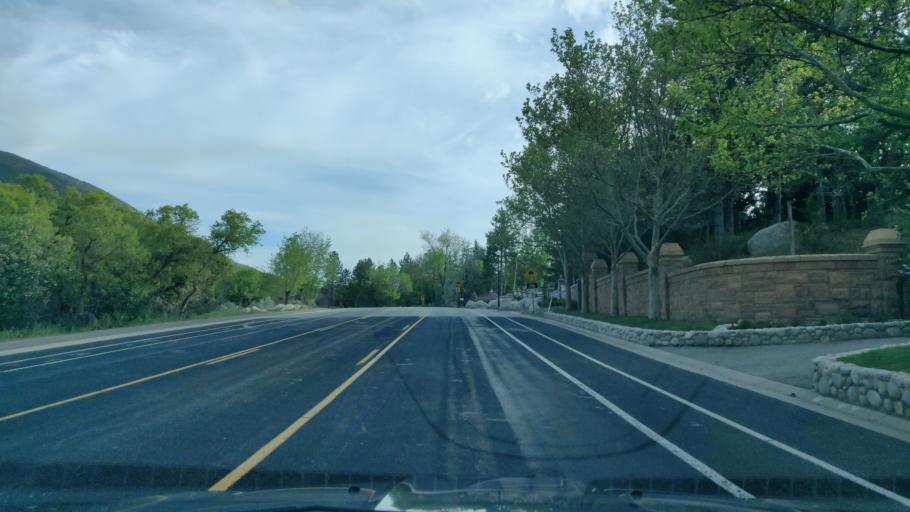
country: US
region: Utah
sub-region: Salt Lake County
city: Granite
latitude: 40.5557
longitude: -111.8026
